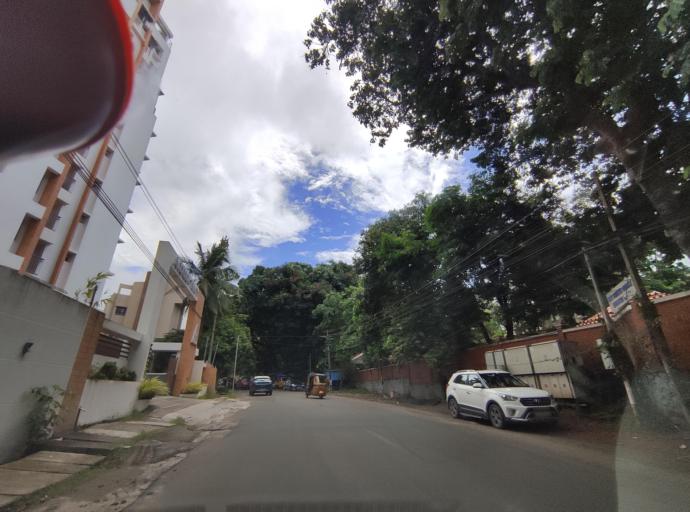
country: IN
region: Kerala
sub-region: Thiruvananthapuram
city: Thiruvananthapuram
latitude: 8.4976
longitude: 76.9613
